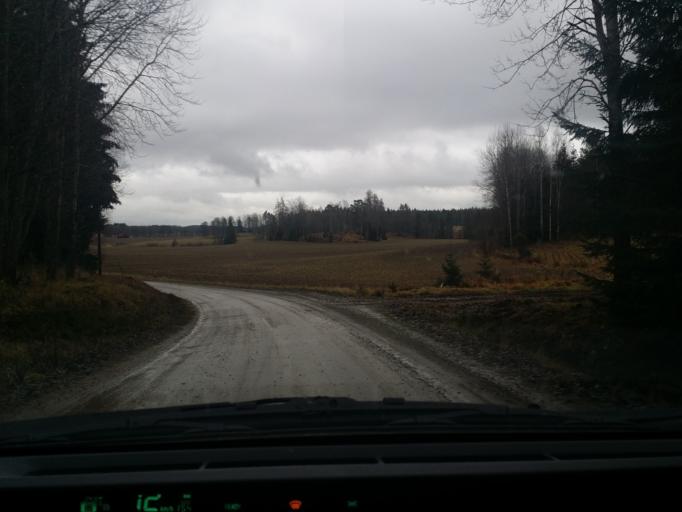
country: SE
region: Vaestmanland
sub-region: Vasteras
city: Skultuna
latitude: 59.7726
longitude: 16.3629
